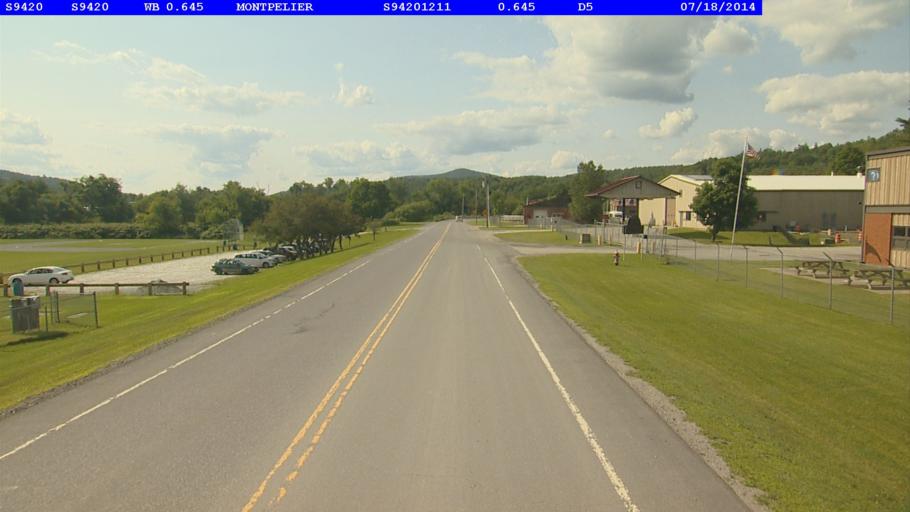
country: US
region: Vermont
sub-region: Washington County
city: Montpelier
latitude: 44.2529
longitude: -72.5997
